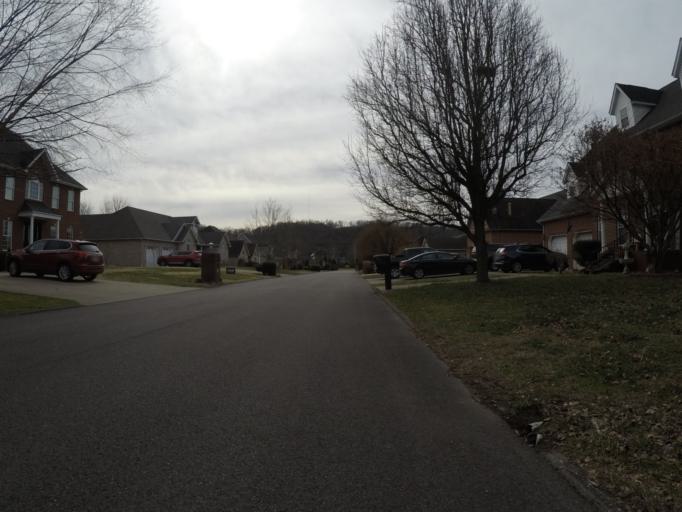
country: US
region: West Virginia
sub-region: Cabell County
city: Pea Ridge
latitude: 38.4434
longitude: -82.3488
